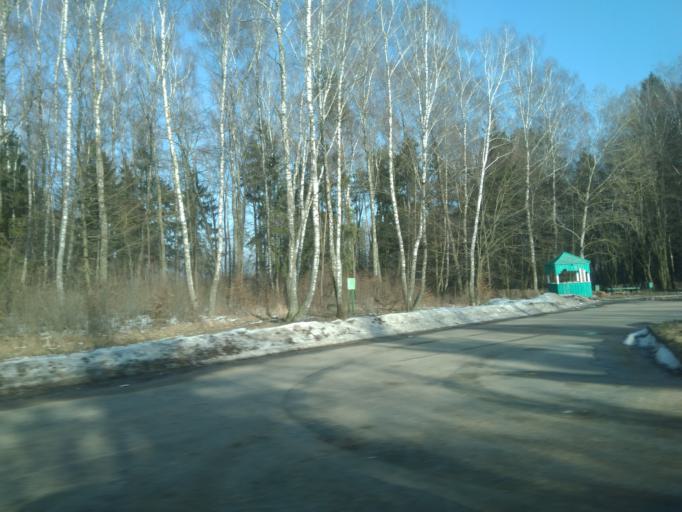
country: BY
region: Minsk
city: Snow
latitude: 53.2158
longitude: 26.4408
